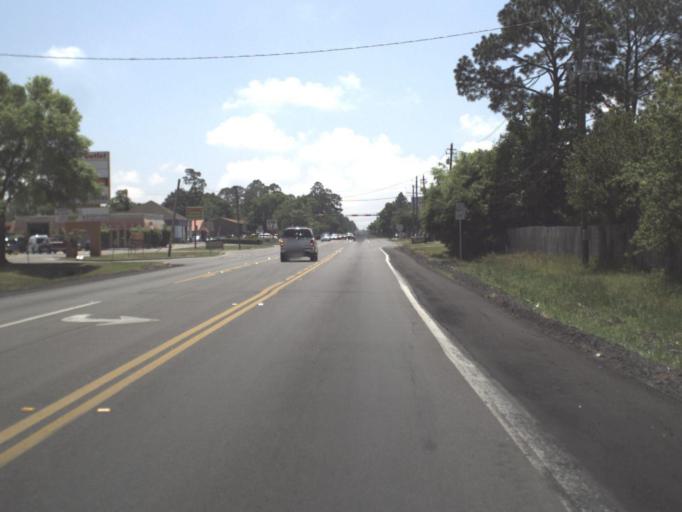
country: US
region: Florida
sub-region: Escambia County
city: Myrtle Grove
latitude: 30.4233
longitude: -87.3173
